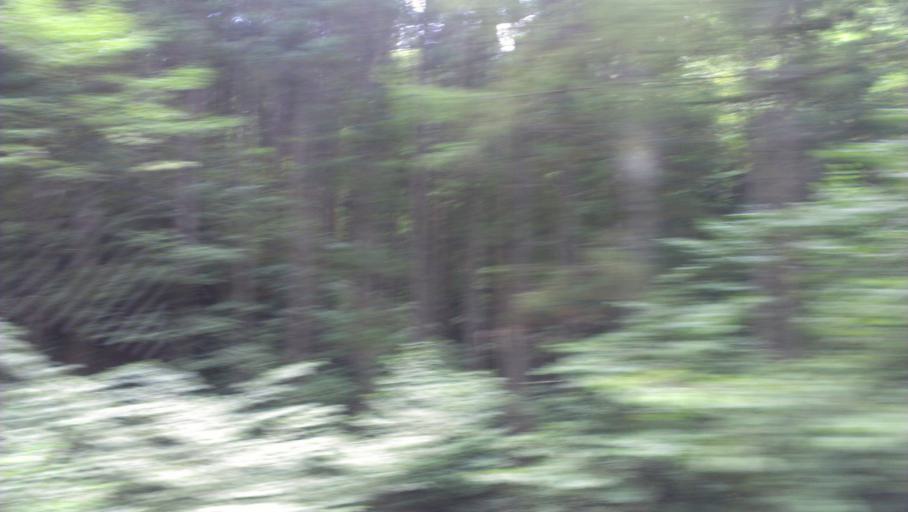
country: JP
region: Fukushima
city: Inawashiro
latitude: 37.4105
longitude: 139.9652
